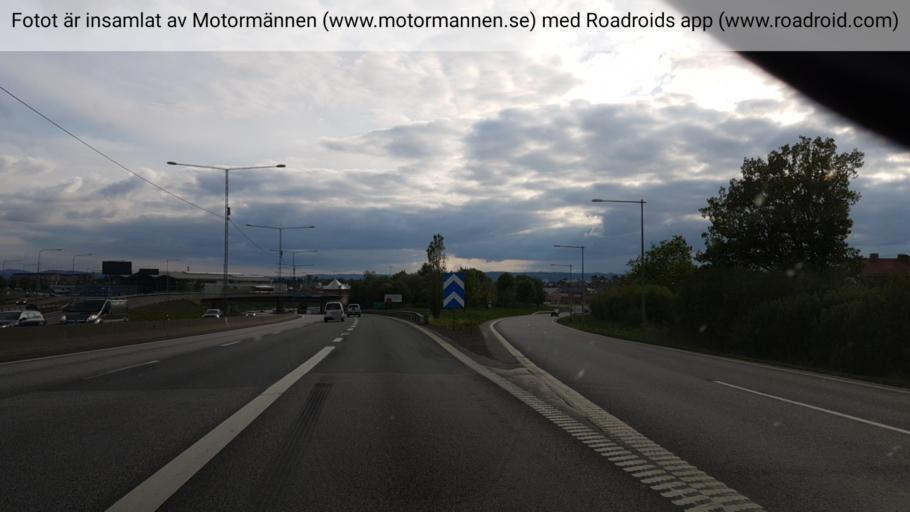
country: SE
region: Joenkoeping
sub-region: Jonkopings Kommun
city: Jonkoping
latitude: 57.7763
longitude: 14.2130
